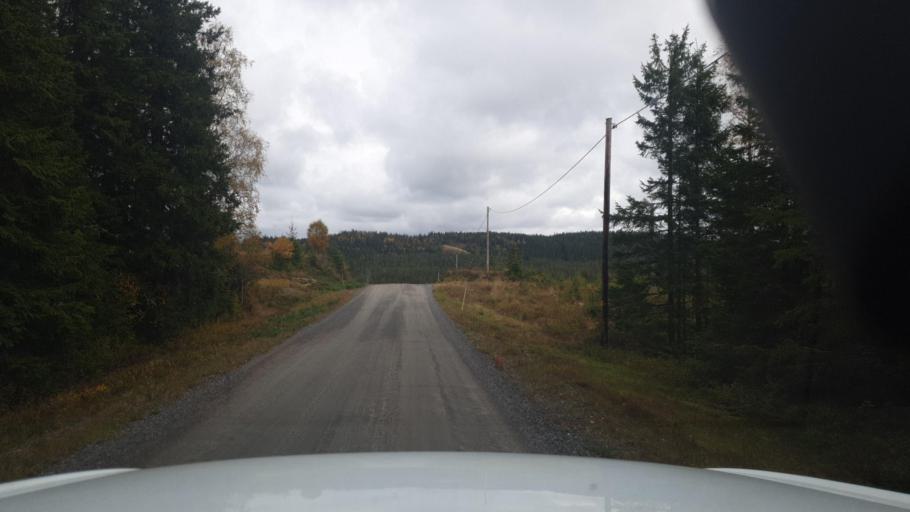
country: SE
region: Vaermland
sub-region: Torsby Kommun
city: Torsby
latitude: 60.1616
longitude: 12.6073
